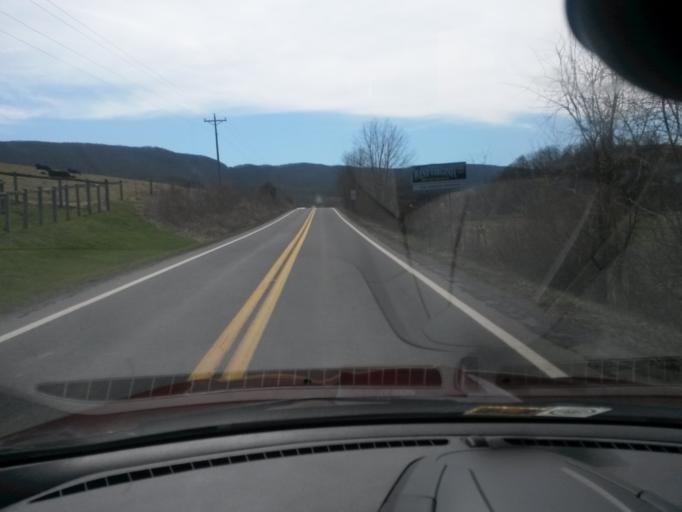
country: US
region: West Virginia
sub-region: Greenbrier County
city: White Sulphur Springs
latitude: 37.6378
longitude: -80.2393
